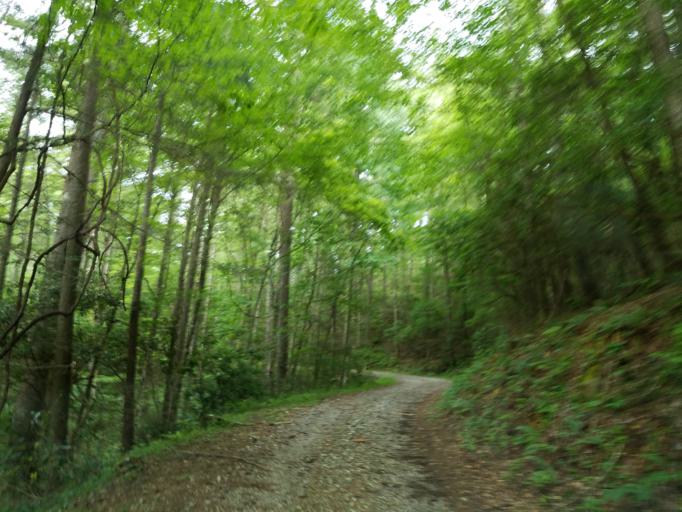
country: US
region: Georgia
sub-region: Union County
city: Blairsville
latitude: 34.7691
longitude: -84.0319
